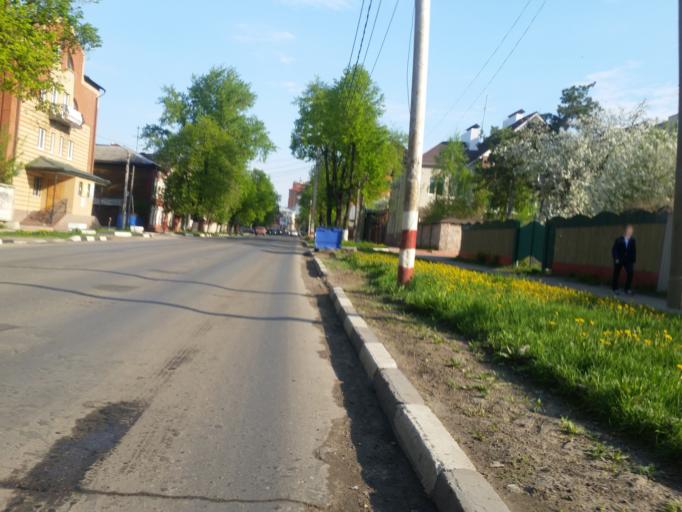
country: RU
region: Ulyanovsk
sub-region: Ulyanovskiy Rayon
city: Ulyanovsk
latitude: 54.3254
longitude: 48.4000
